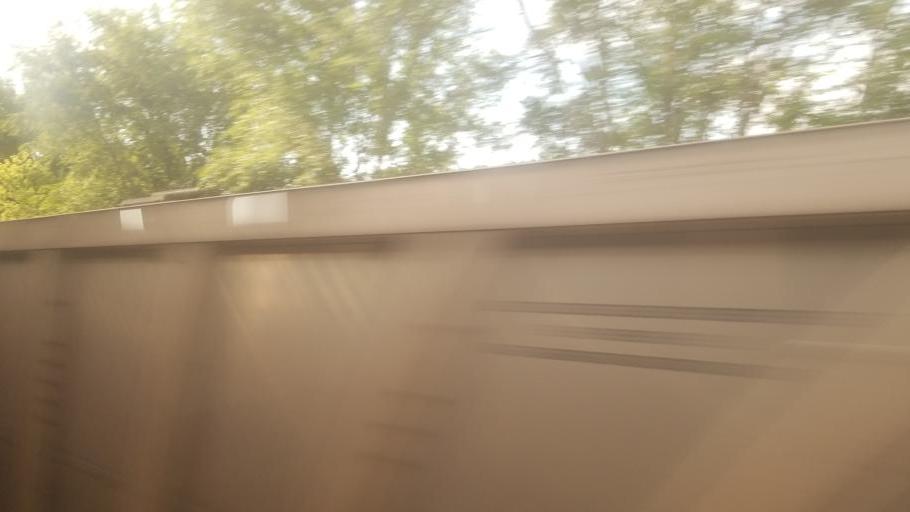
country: US
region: Kansas
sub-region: Johnson County
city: De Soto
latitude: 38.9811
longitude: -94.9427
